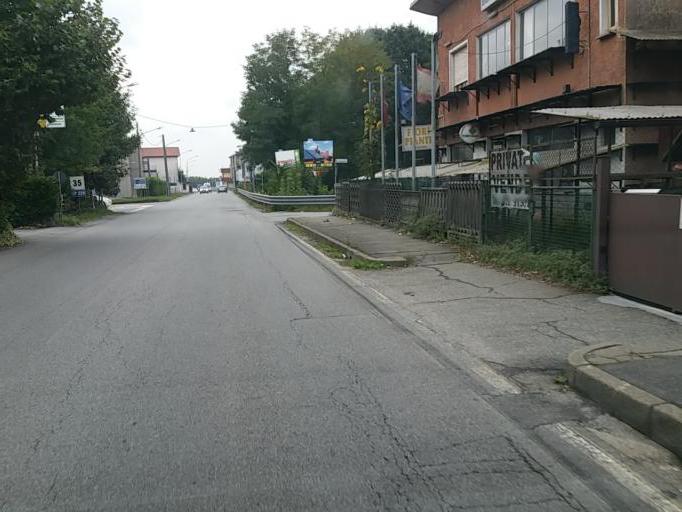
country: IT
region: Piedmont
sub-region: Provincia di Novara
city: Briga Novarese
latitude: 45.7297
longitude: 8.4438
